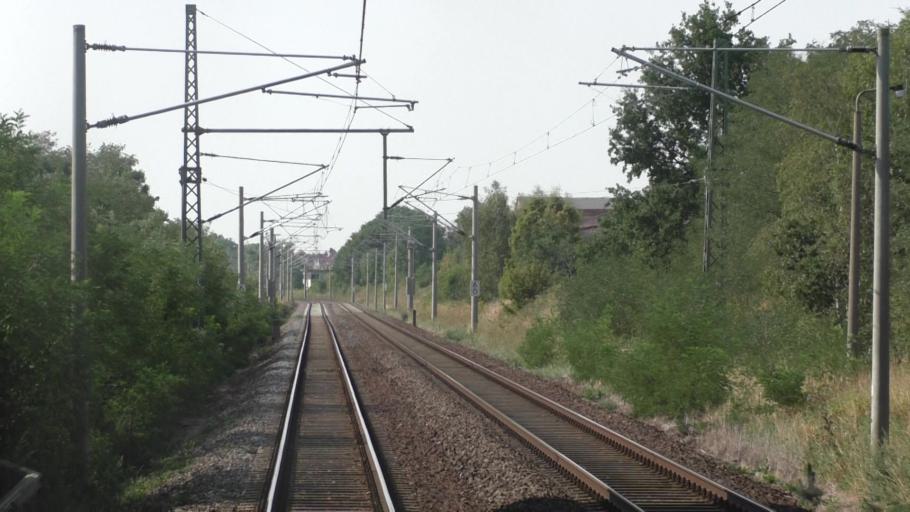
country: DE
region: Saxony-Anhalt
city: Zerbst
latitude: 51.9467
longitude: 12.1042
